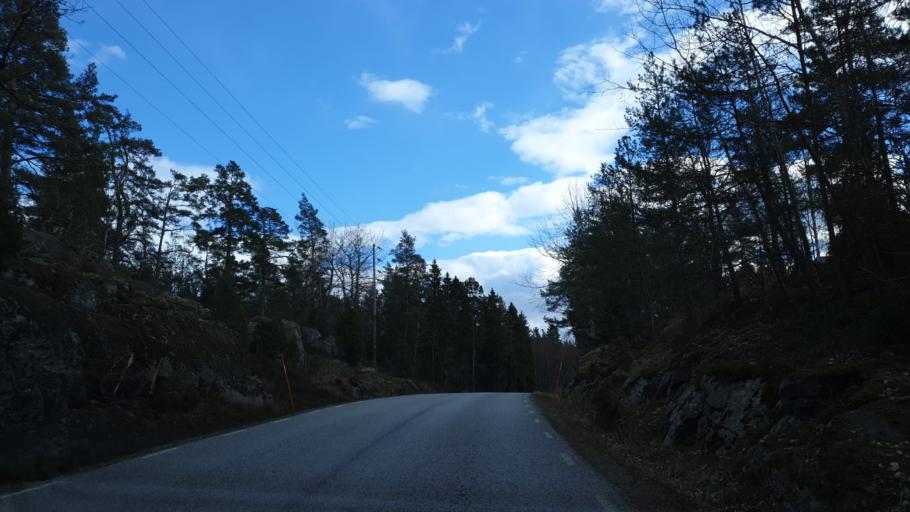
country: SE
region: Stockholm
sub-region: Varmdo Kommun
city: Hemmesta
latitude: 59.2306
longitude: 18.4841
